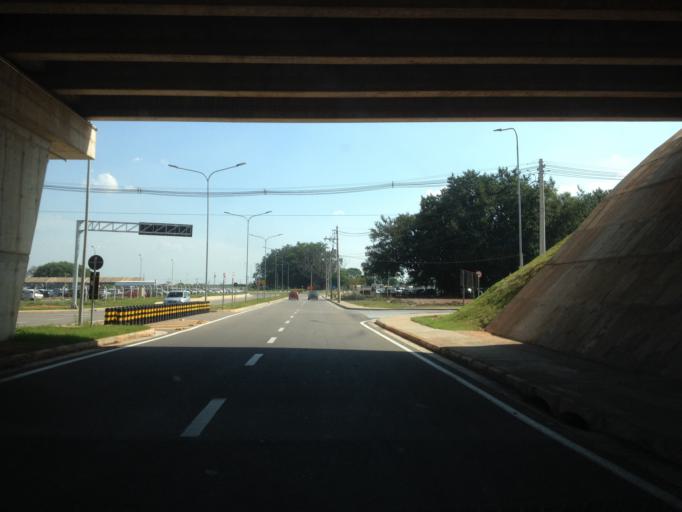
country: BR
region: Sao Paulo
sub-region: Indaiatuba
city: Indaiatuba
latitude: -23.0142
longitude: -47.1409
